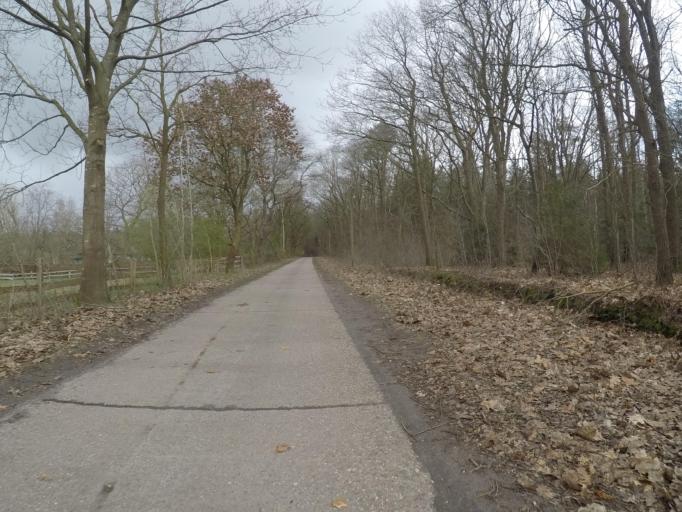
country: DE
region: Lower Saxony
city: Elmlohe
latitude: 53.6074
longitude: 8.7280
